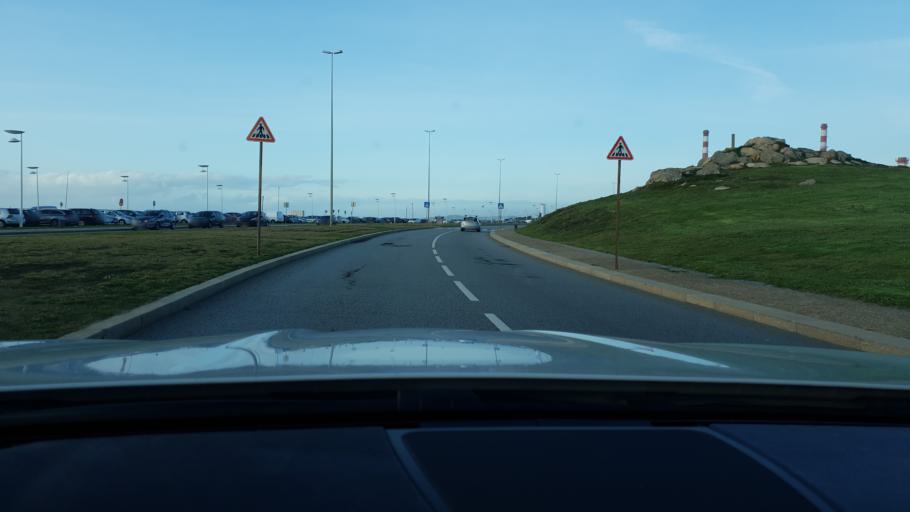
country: PT
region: Porto
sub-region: Matosinhos
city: Leca da Palmeira
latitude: 41.2065
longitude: -8.7146
